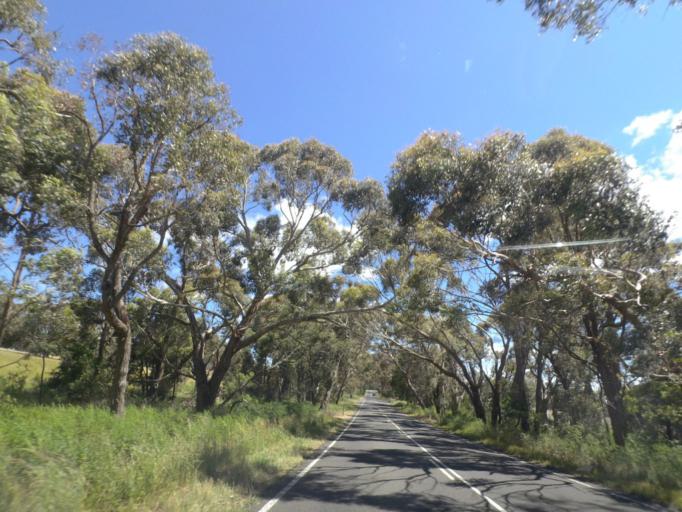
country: AU
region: Victoria
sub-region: Mount Alexander
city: Castlemaine
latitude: -37.3099
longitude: 144.4121
